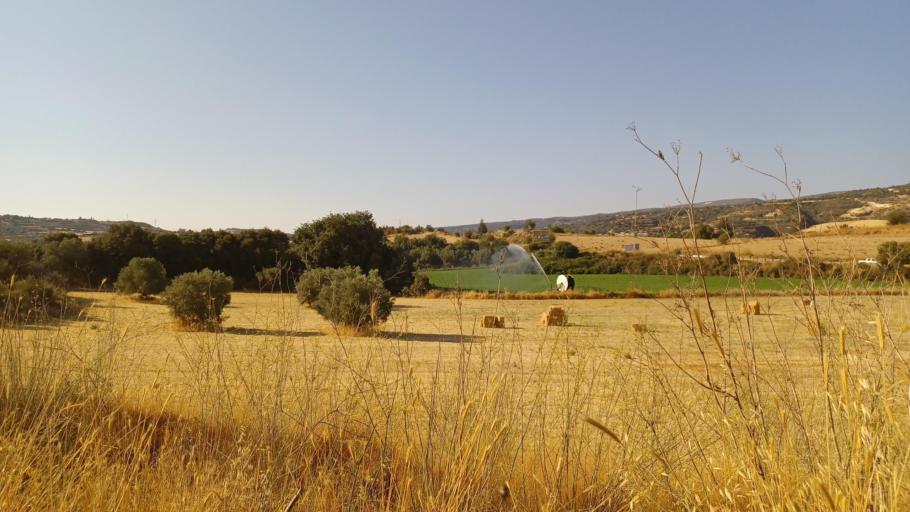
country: CY
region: Pafos
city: Polis
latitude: 35.0048
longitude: 32.4440
